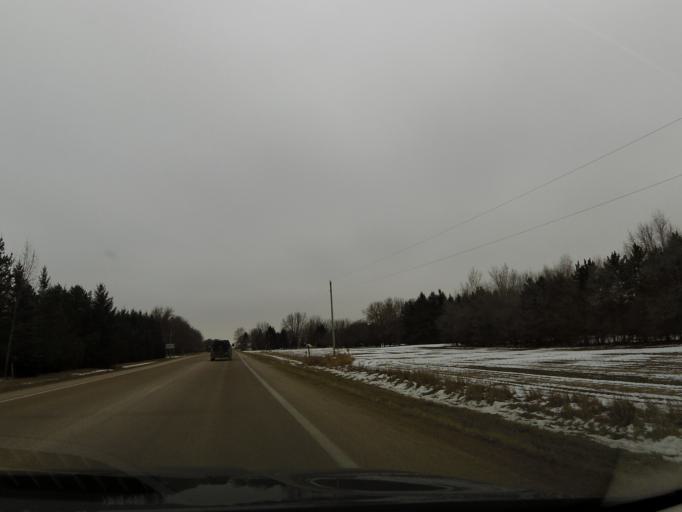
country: US
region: Minnesota
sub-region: Carver County
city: Carver
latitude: 44.7174
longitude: -93.6485
